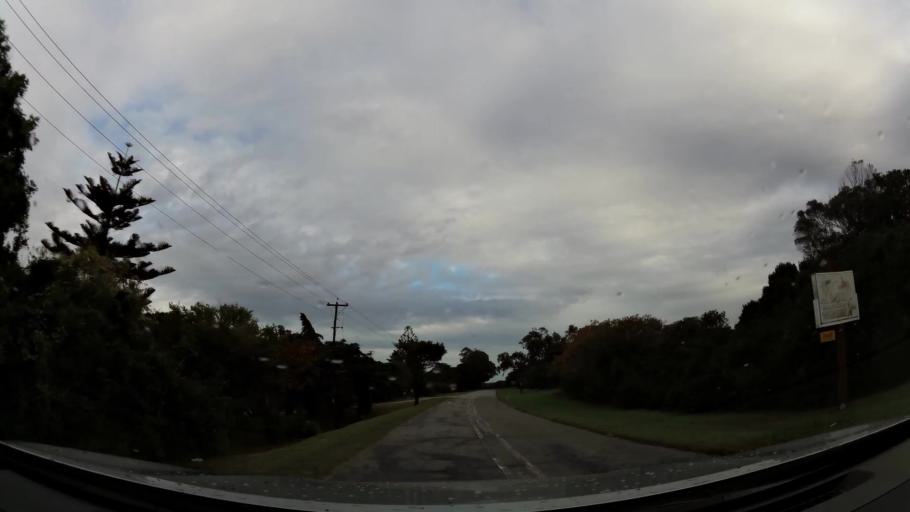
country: ZA
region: Eastern Cape
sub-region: Nelson Mandela Bay Metropolitan Municipality
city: Port Elizabeth
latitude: -34.0164
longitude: 25.5058
